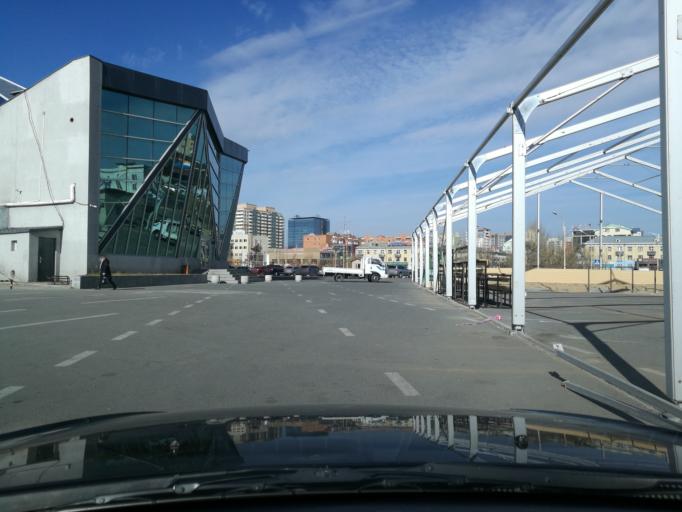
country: MN
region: Ulaanbaatar
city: Ulaanbaatar
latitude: 47.9120
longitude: 106.9080
